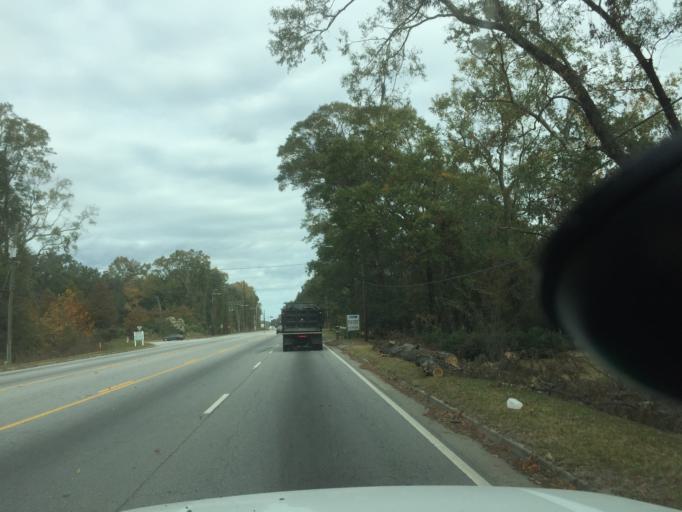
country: US
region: Georgia
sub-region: Chatham County
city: Garden City
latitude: 32.0990
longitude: -81.1961
